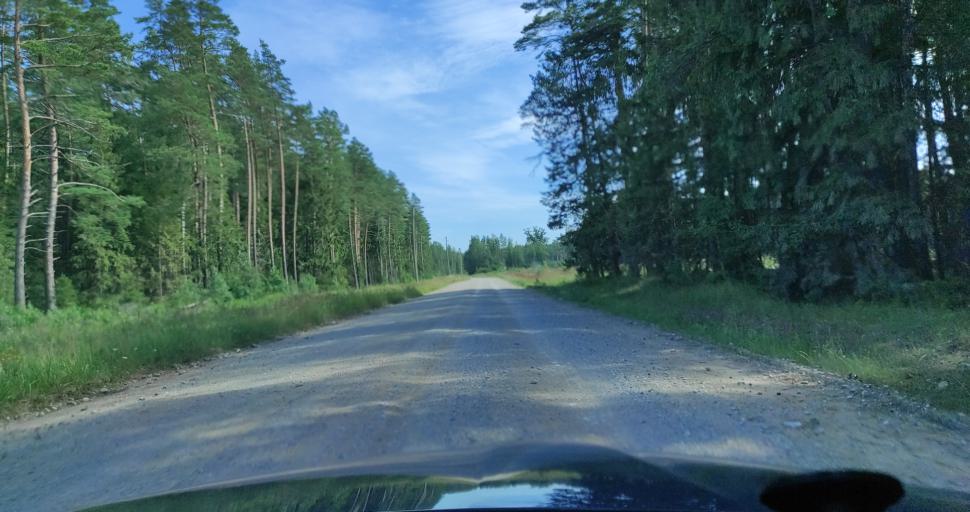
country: LV
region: Durbe
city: Liegi
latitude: 56.7616
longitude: 21.3207
